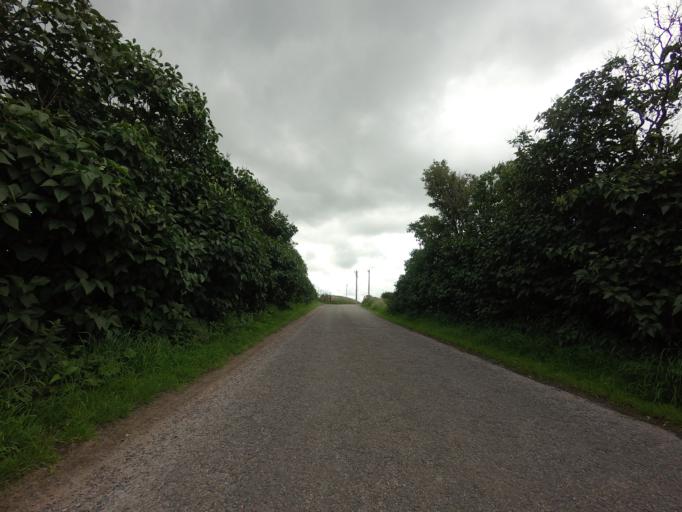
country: GB
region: Scotland
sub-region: Moray
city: Kinloss
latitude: 57.6356
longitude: -3.5182
